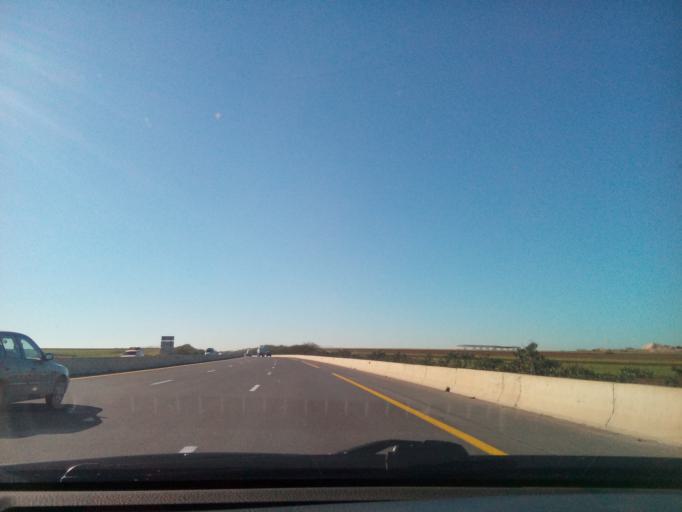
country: DZ
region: Relizane
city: Djidiouia
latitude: 35.8951
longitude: 0.7087
